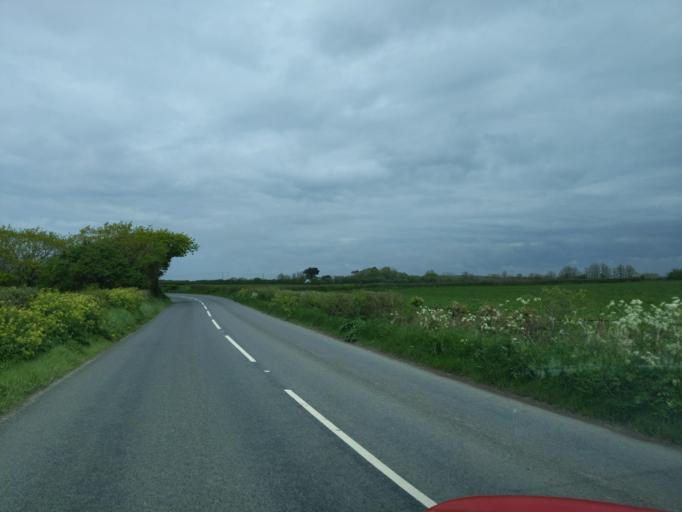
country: GB
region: England
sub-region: Cornwall
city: Wadebridge
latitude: 50.5557
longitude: -4.8641
